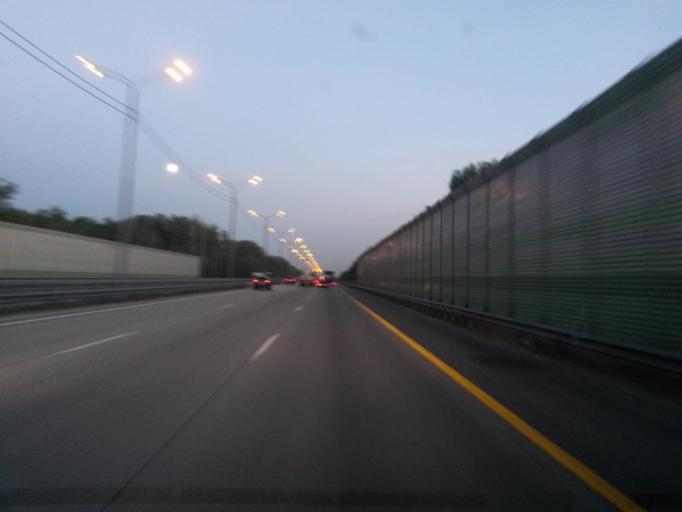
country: RU
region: Moskovskaya
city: Belyye Stolby
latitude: 55.3046
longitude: 37.8313
